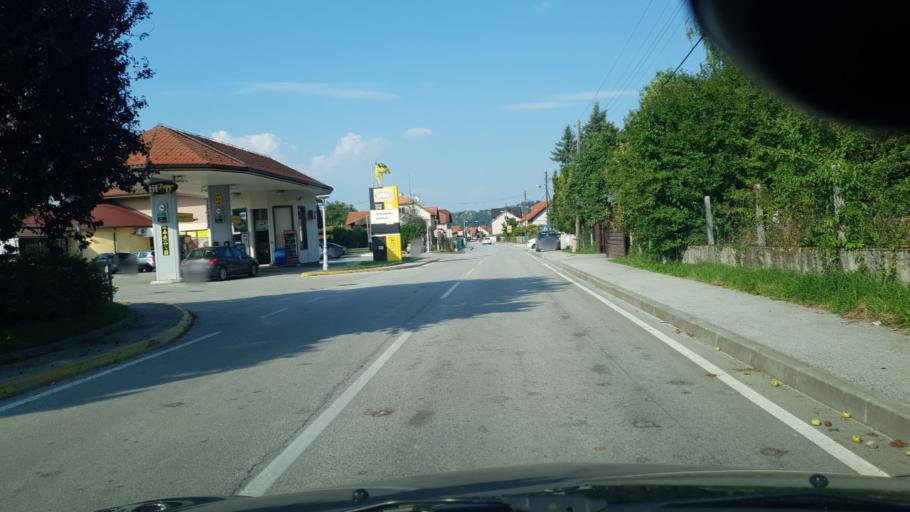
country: HR
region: Krapinsko-Zagorska
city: Oroslavje
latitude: 45.9738
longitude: 15.9205
